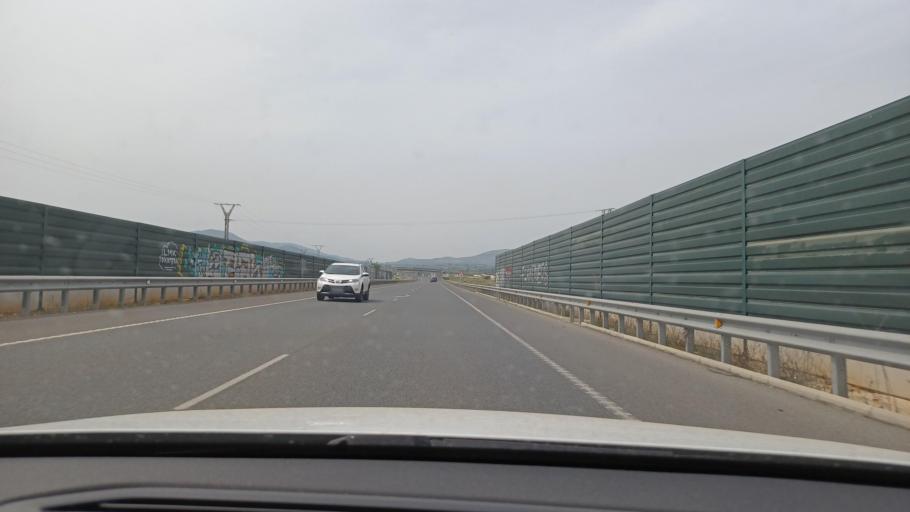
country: ES
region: Valencia
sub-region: Provincia de Castello
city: Benicarlo
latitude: 40.4272
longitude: 0.3983
